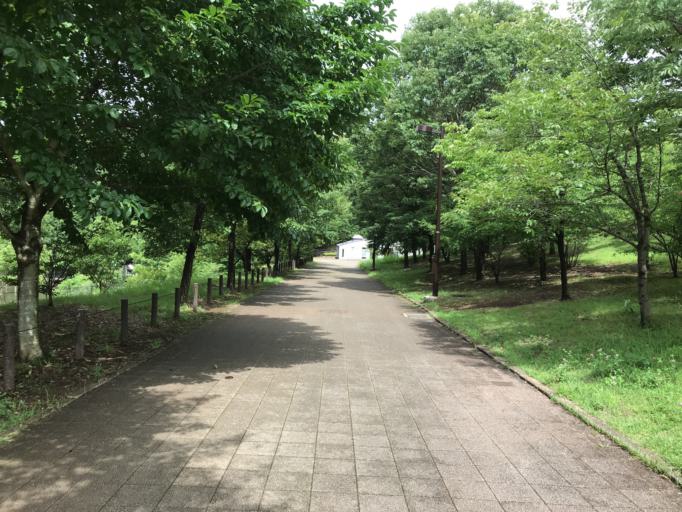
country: JP
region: Tokyo
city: Hachioji
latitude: 35.6076
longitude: 139.3673
